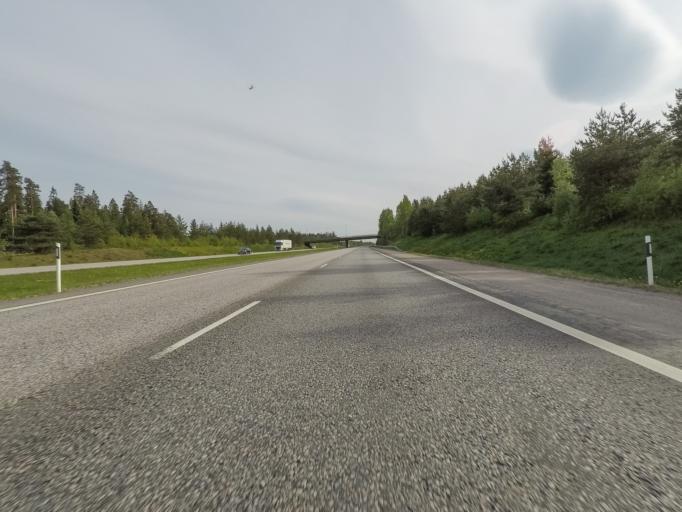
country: FI
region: Uusimaa
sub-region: Helsinki
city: Nurmijaervi
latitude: 60.4582
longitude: 24.8473
